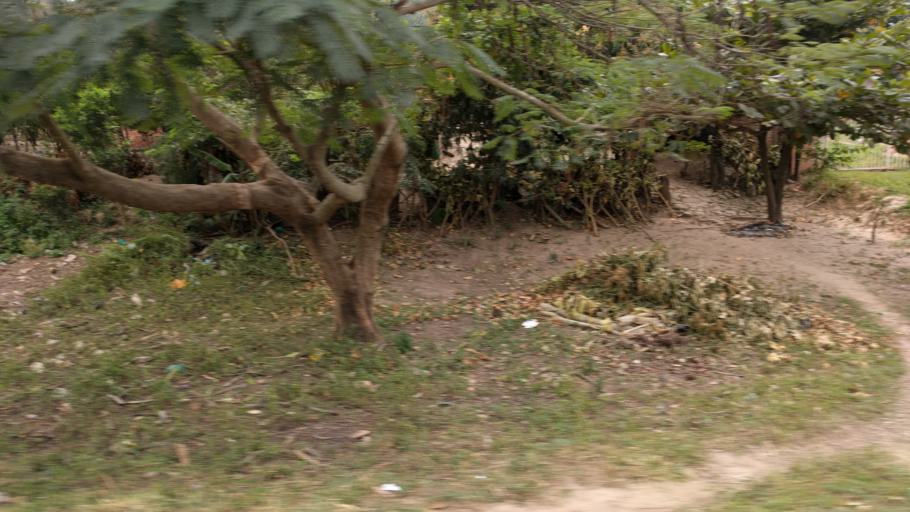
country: BO
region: Santa Cruz
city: Jorochito
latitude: -18.1545
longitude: -63.4960
